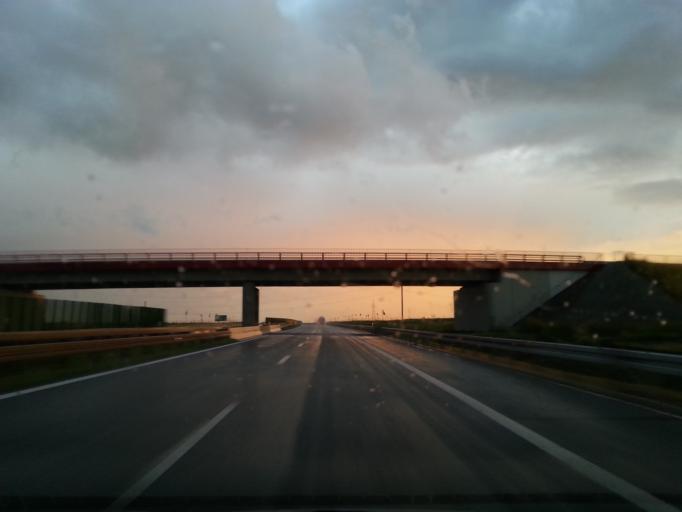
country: PL
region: Lower Silesian Voivodeship
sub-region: Powiat wroclawski
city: Mirkow
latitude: 51.2156
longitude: 17.1363
